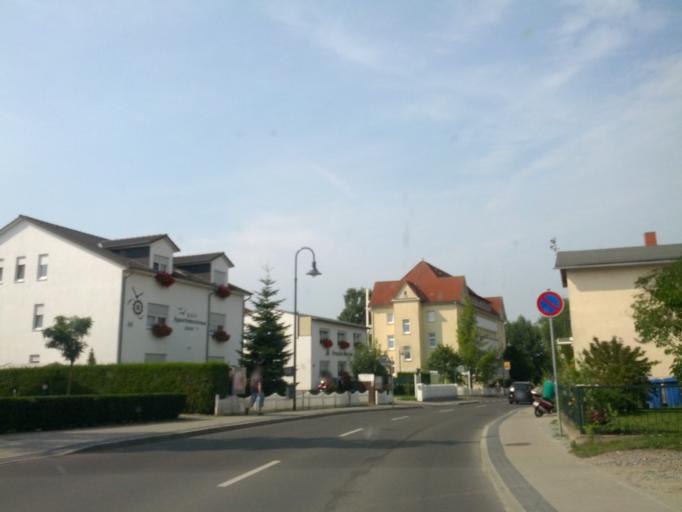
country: DE
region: Mecklenburg-Vorpommern
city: Ostseebad Binz
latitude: 54.3946
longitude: 13.6075
